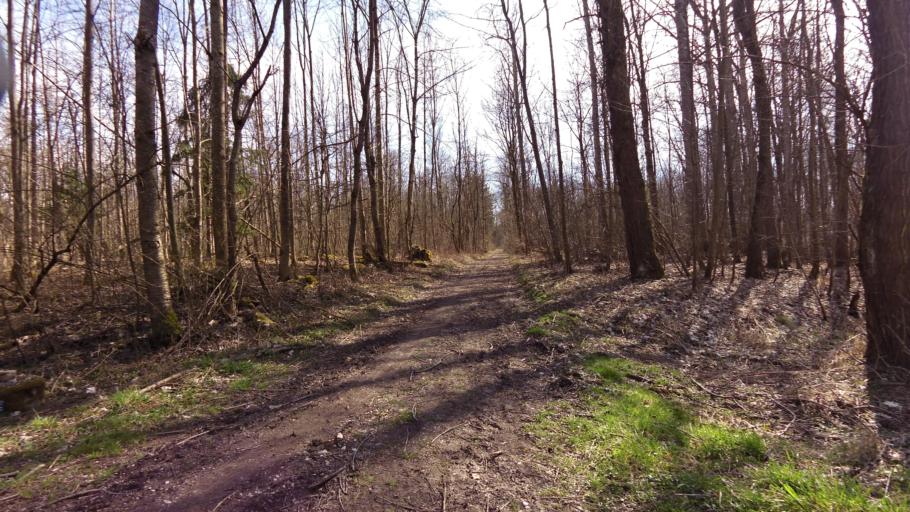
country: DE
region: Bavaria
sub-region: Lower Bavaria
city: Tiefenbach
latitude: 48.5189
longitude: 12.0882
